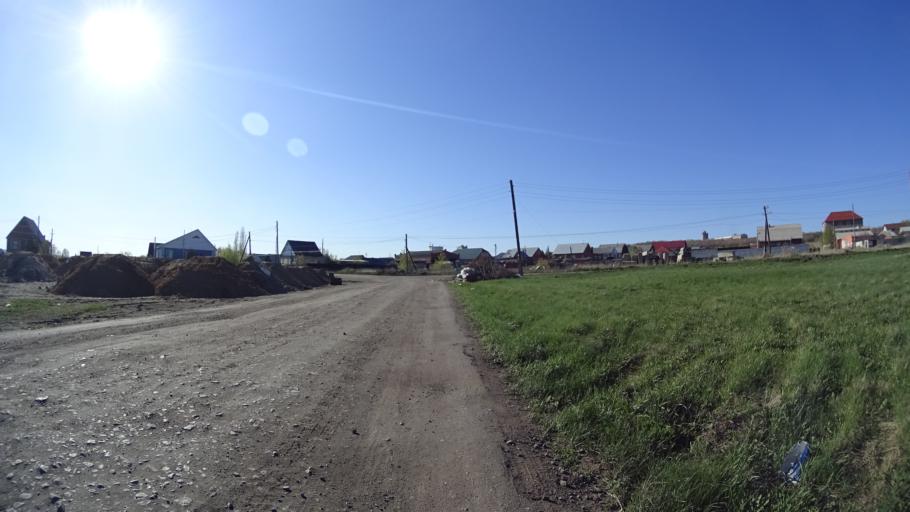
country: RU
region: Chelyabinsk
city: Troitsk
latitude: 54.0957
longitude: 61.5980
